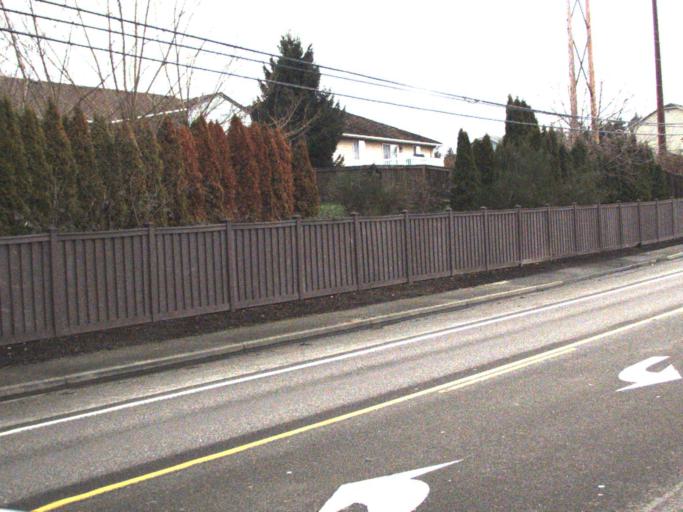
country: US
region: Washington
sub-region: Snohomish County
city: Sisco Heights
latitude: 48.1518
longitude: -122.1260
